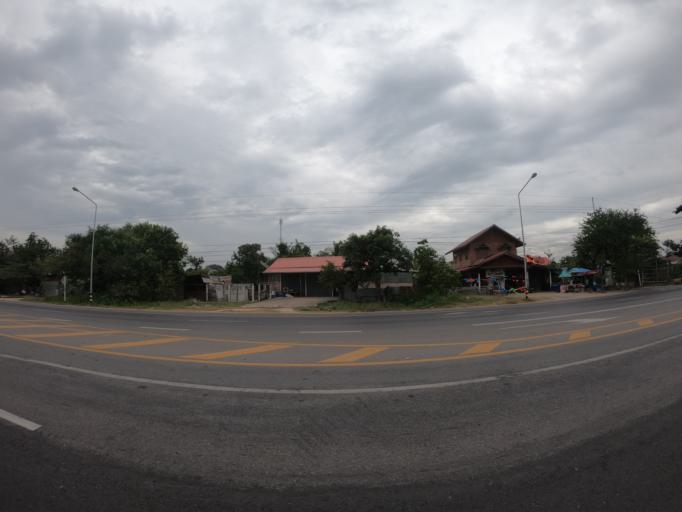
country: TH
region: Roi Et
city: Chiang Khwan
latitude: 16.1010
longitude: 103.8036
